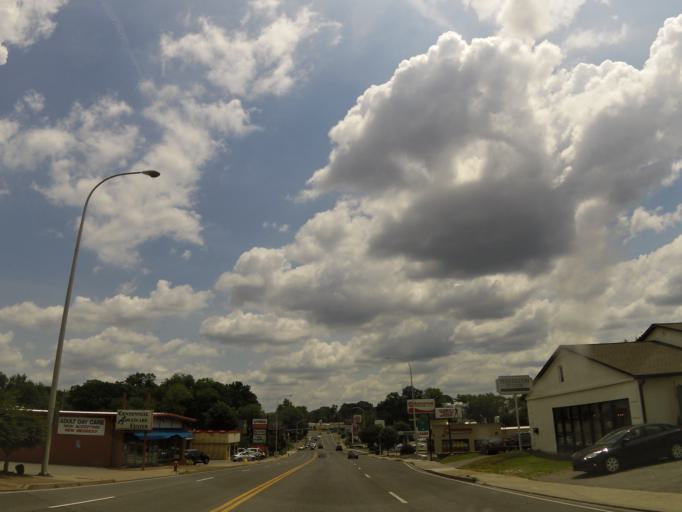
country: US
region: Tennessee
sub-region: Davidson County
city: Nashville
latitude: 36.1359
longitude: -86.7789
